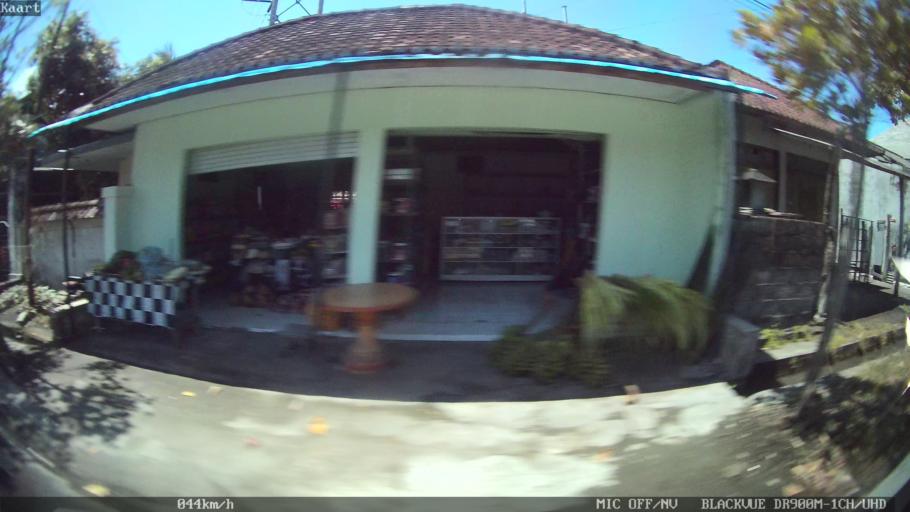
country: ID
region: Bali
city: Banjar Pasekan
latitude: -8.5704
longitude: 115.3219
